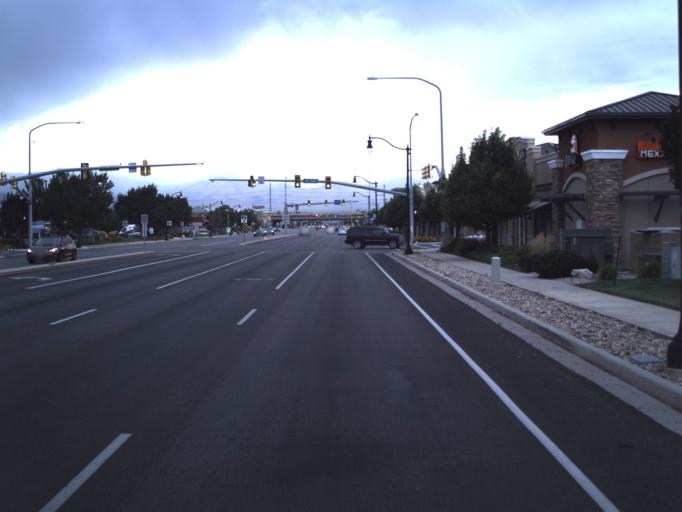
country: US
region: Utah
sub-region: Salt Lake County
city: Draper
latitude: 40.5269
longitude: -111.8841
